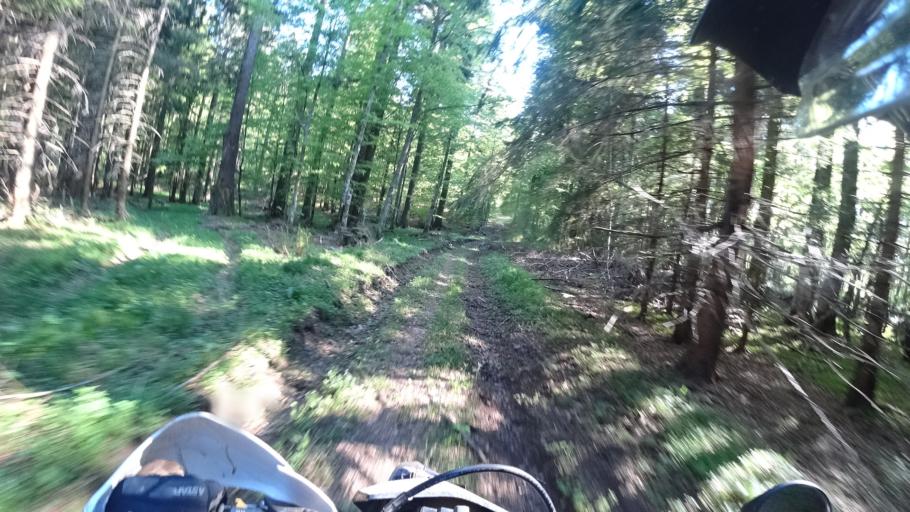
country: HR
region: Primorsko-Goranska
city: Vrbovsko
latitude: 45.2857
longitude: 14.9511
